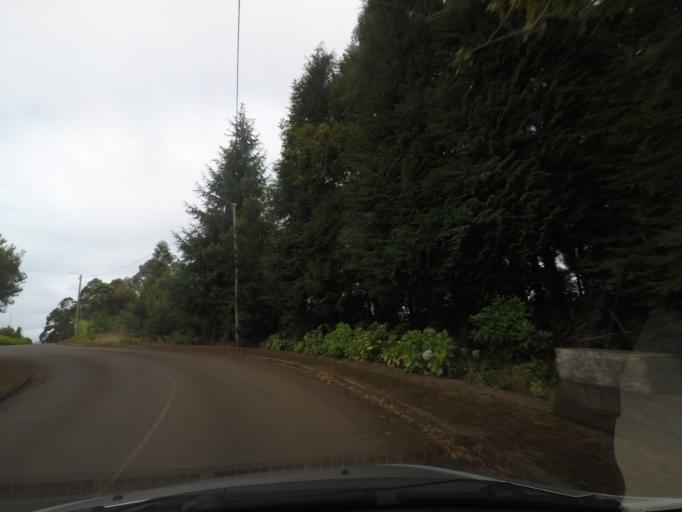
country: PT
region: Madeira
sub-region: Santana
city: Santana
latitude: 32.7852
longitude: -16.8788
